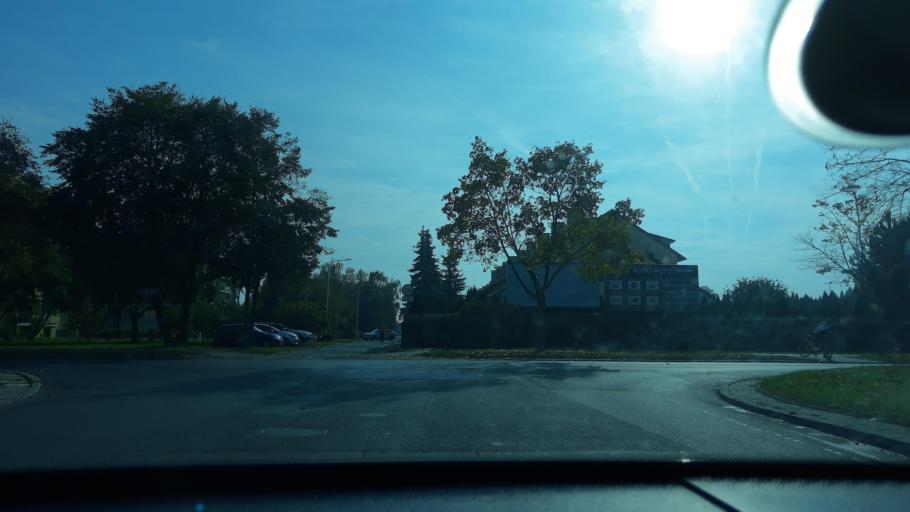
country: PL
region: Lodz Voivodeship
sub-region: Powiat sieradzki
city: Sieradz
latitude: 51.5875
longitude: 18.7139
